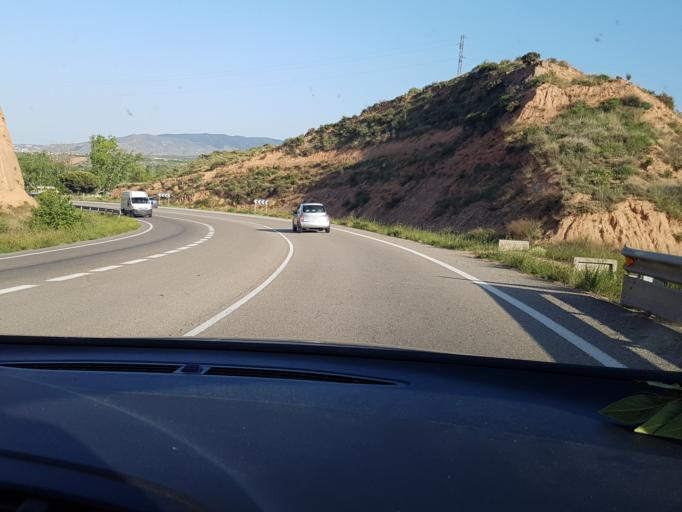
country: ES
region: La Rioja
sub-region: Provincia de La Rioja
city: Arnedo
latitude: 42.2333
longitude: -2.0814
